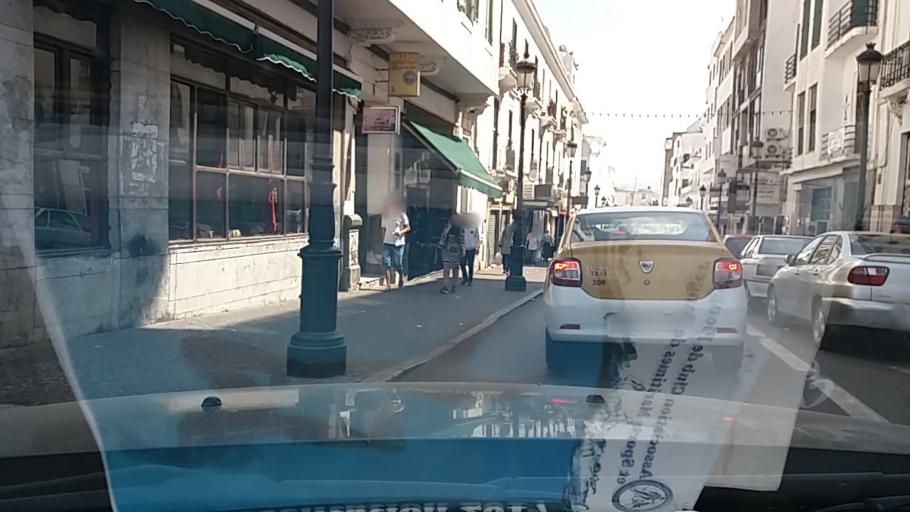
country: MA
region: Tanger-Tetouan
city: Tetouan
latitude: 35.5699
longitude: -5.3740
